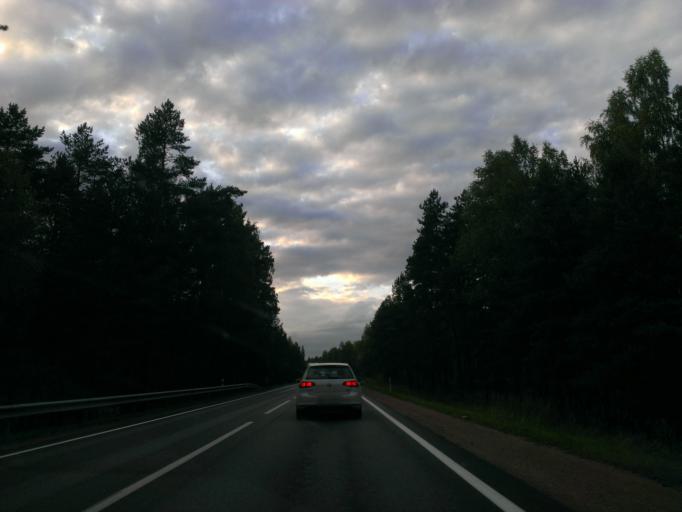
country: LV
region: Riga
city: Bergi
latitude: 56.9600
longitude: 24.3752
